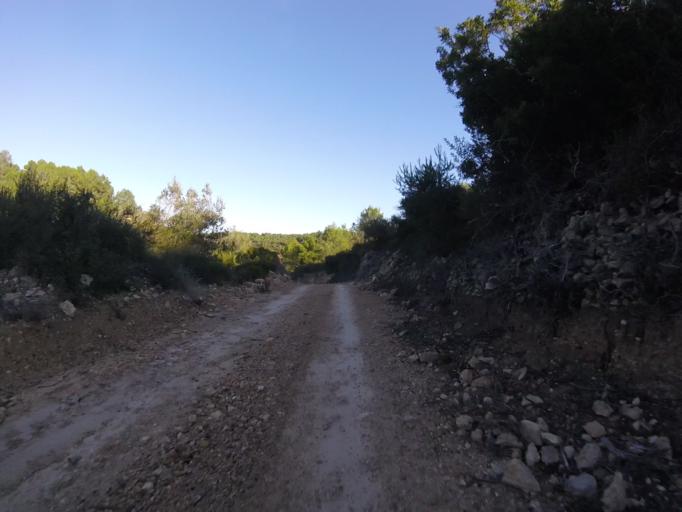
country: ES
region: Valencia
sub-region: Provincia de Castello
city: Torreblanca
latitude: 40.2562
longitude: 0.1918
